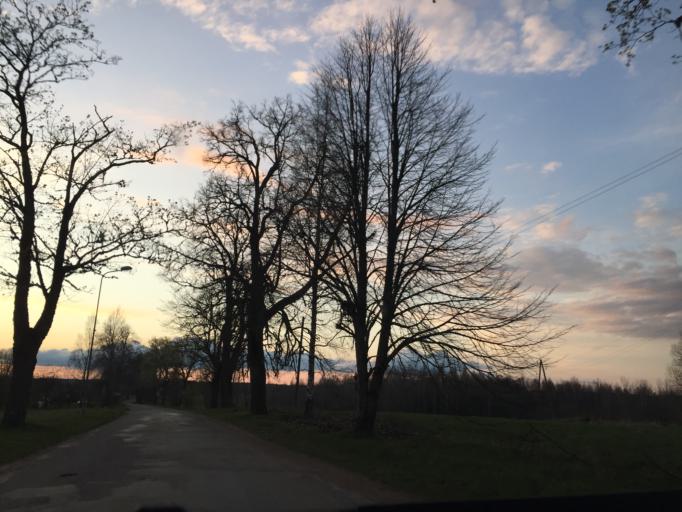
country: LV
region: Aluksnes Rajons
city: Aluksne
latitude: 57.2760
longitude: 26.9256
